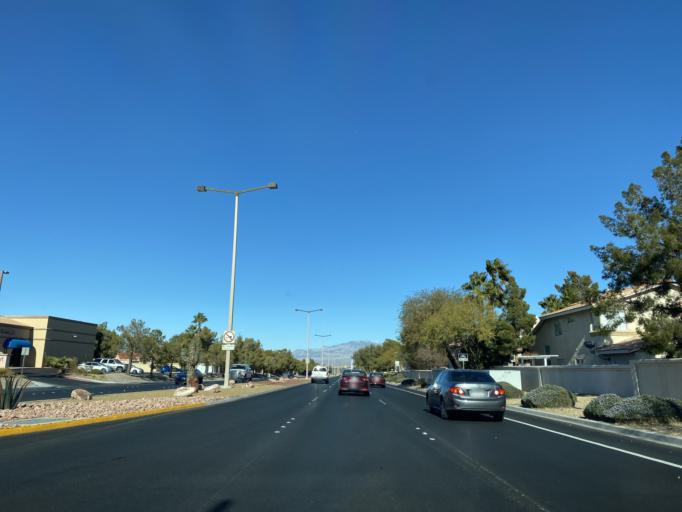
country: US
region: Nevada
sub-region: Clark County
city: Summerlin South
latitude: 36.2102
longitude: -115.2788
